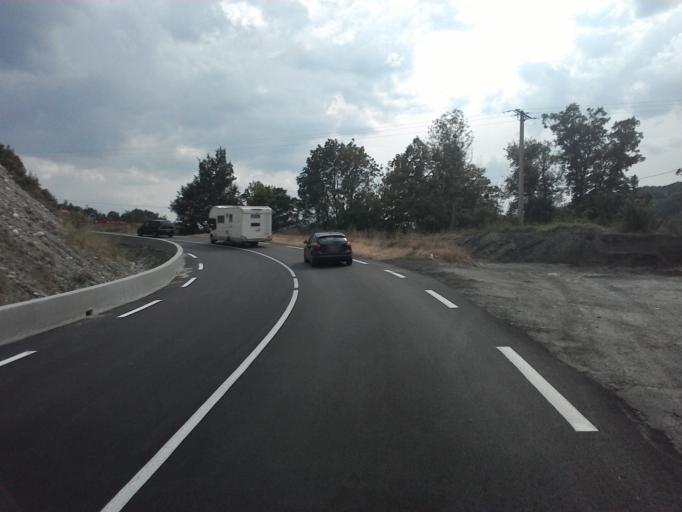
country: FR
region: Rhone-Alpes
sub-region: Departement de l'Isere
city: La Mure
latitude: 44.8972
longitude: 5.8168
